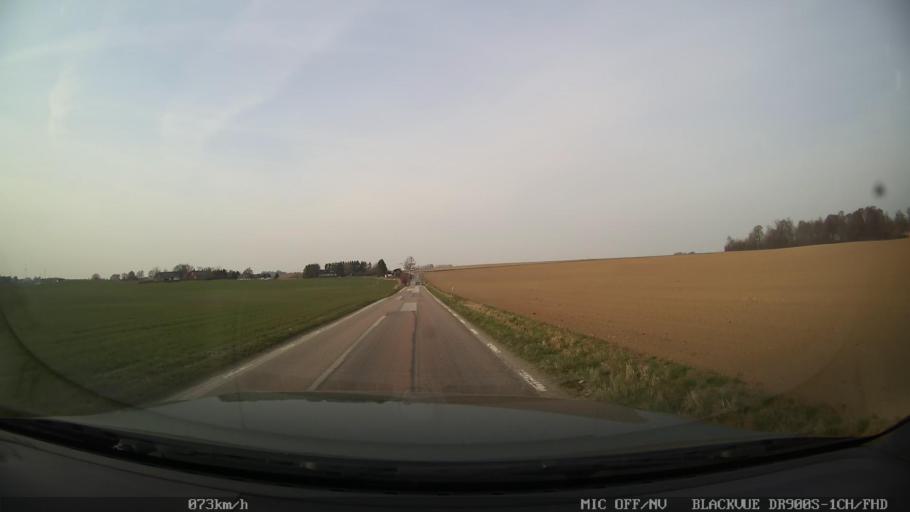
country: SE
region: Skane
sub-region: Ystads Kommun
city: Ystad
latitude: 55.4515
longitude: 13.8310
